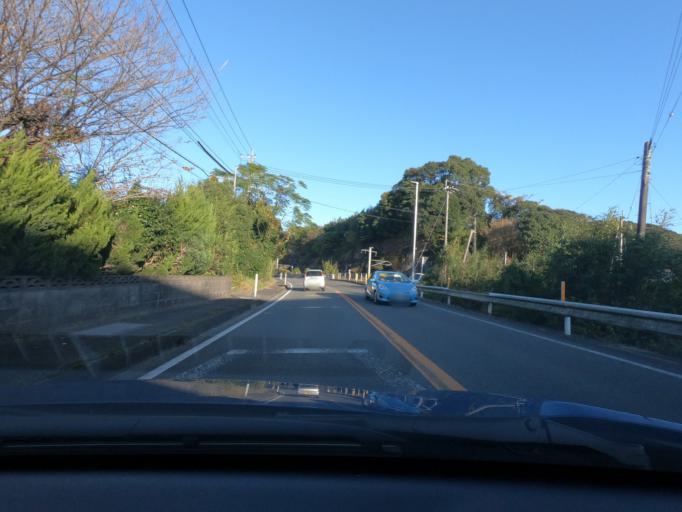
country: JP
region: Kagoshima
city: Satsumasendai
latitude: 31.8472
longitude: 130.2567
